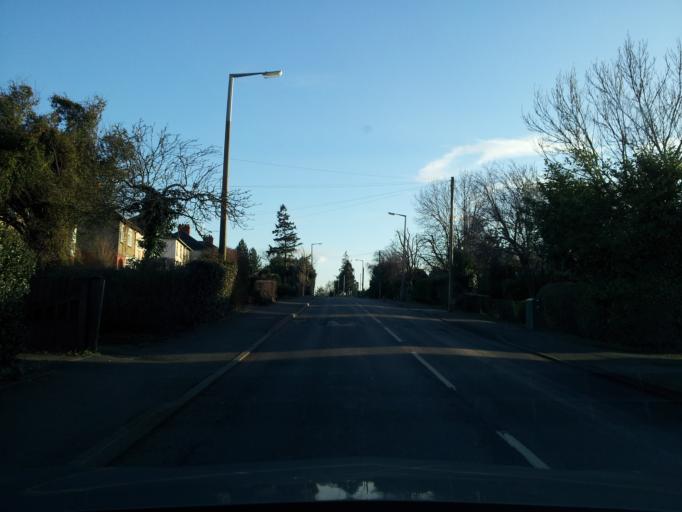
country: GB
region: England
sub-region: Northamptonshire
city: Northampton
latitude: 52.2520
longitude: -0.9513
